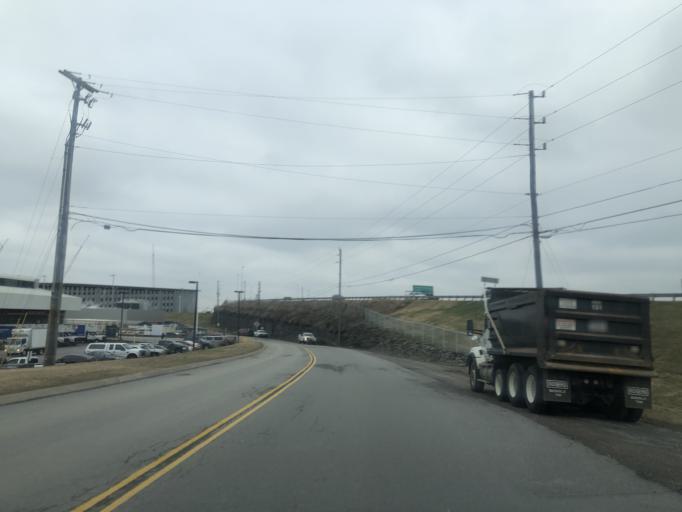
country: US
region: Tennessee
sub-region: Davidson County
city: Lakewood
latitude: 36.1269
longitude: -86.6658
